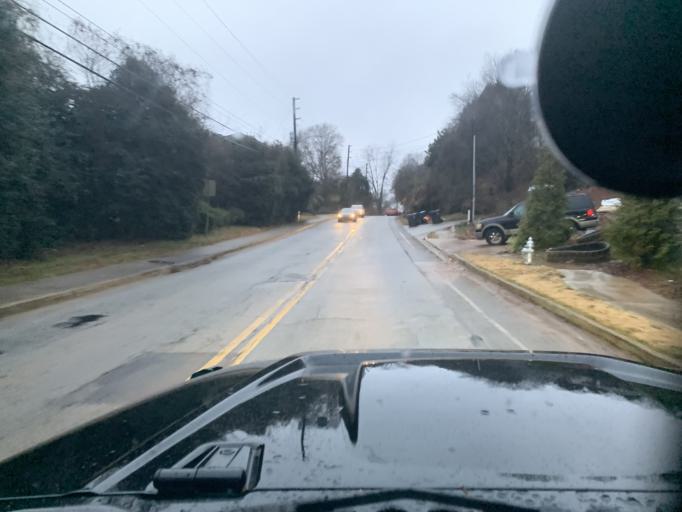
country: US
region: Georgia
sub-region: Fulton County
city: Roswell
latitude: 34.0173
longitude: -84.3588
